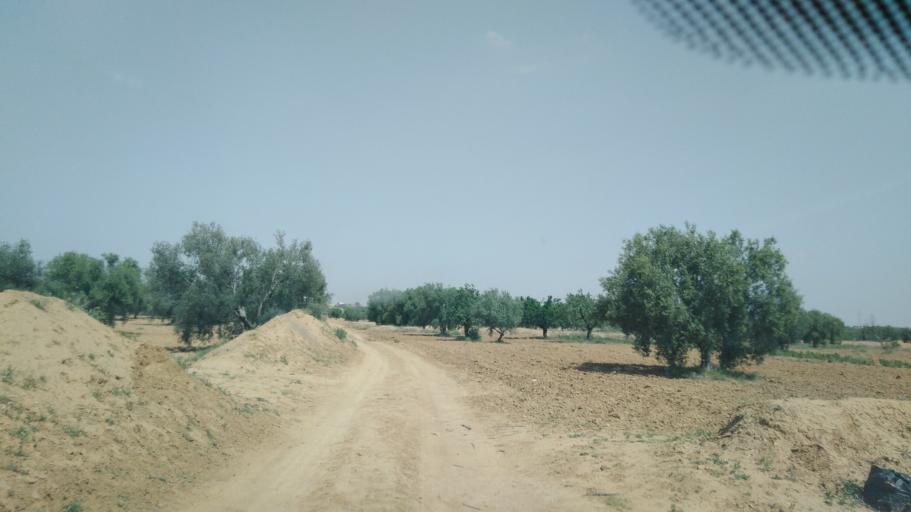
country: TN
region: Safaqis
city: Sfax
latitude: 34.7353
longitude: 10.5743
